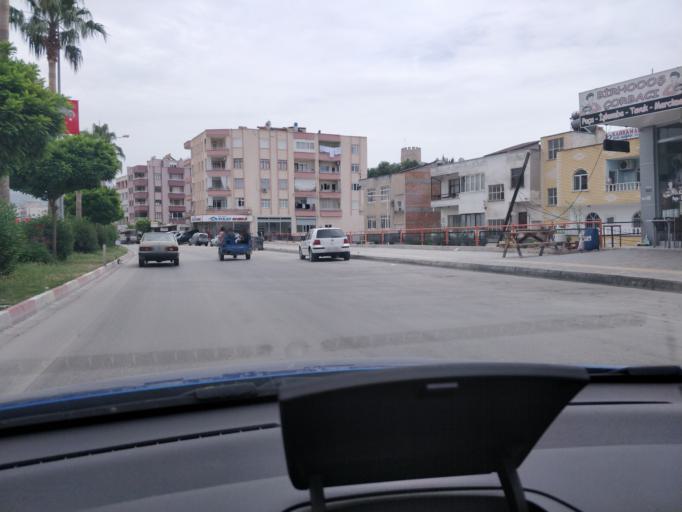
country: TR
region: Mersin
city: Mut
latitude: 36.6458
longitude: 33.4308
